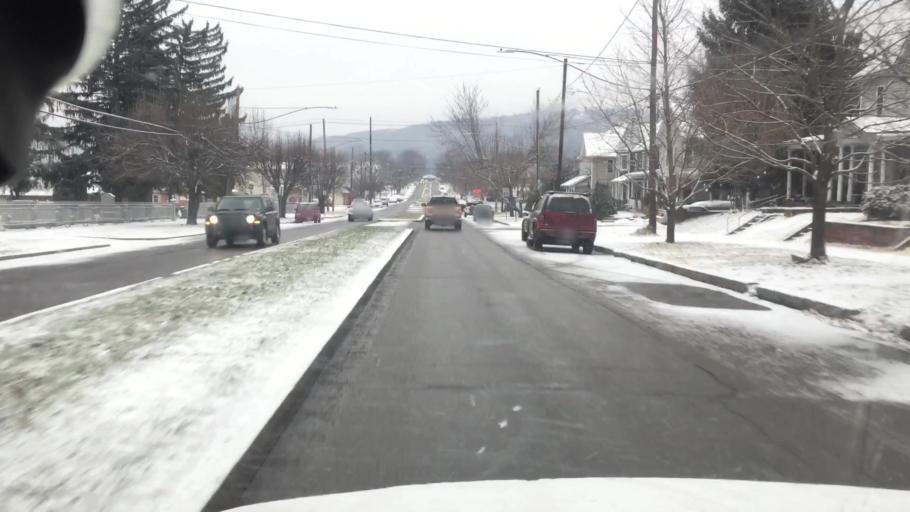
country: US
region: Pennsylvania
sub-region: Columbia County
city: Berwick
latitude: 41.0589
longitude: -76.2371
